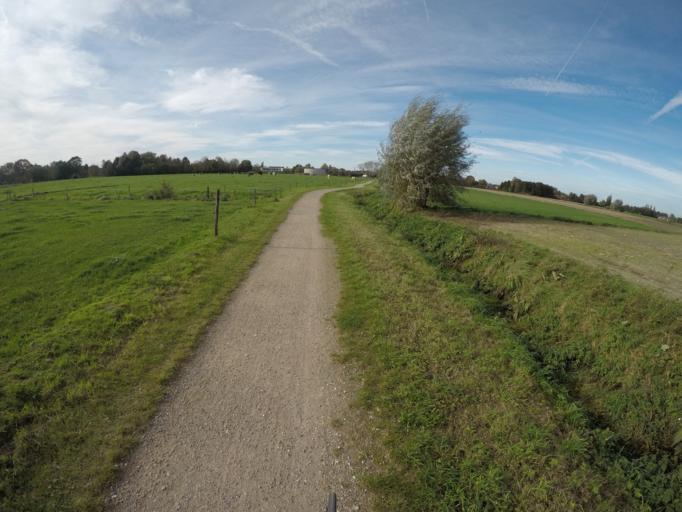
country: BE
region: Flanders
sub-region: Provincie Oost-Vlaanderen
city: Waasmunster
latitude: 51.1550
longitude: 4.0595
